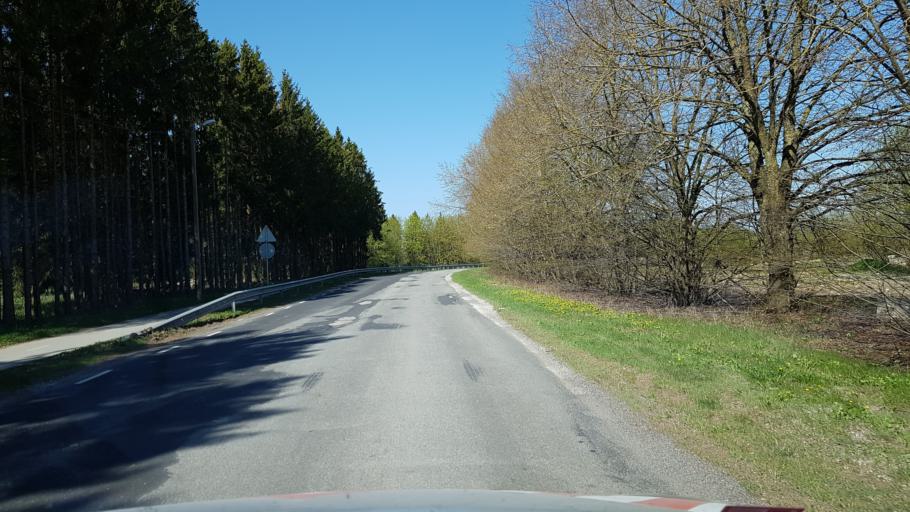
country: EE
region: Harju
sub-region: Joelaehtme vald
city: Loo
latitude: 59.4170
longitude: 24.9438
